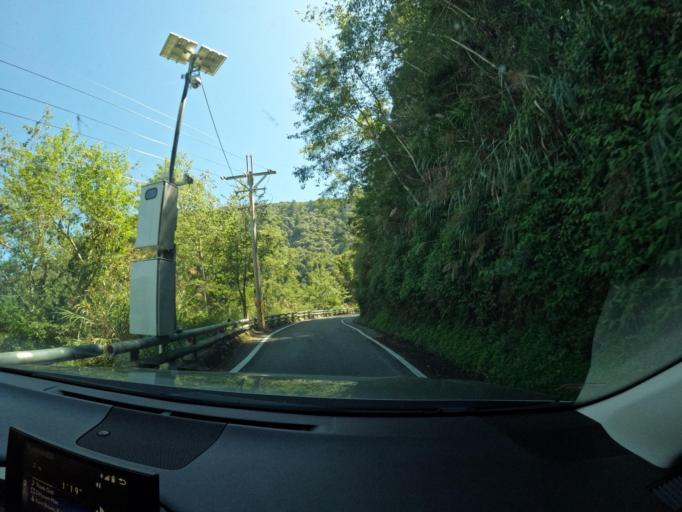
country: TW
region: Taiwan
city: Yujing
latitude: 23.2801
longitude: 120.9069
